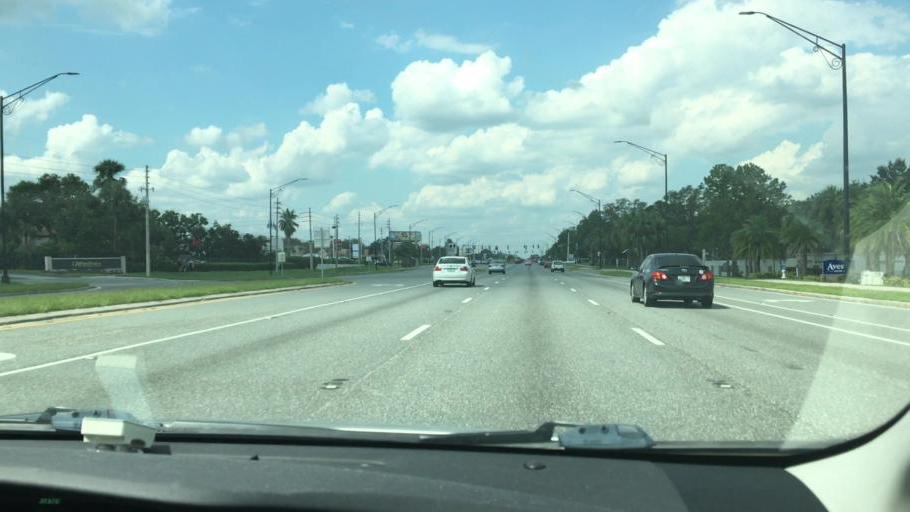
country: US
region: Florida
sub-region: Orange County
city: Conway
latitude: 28.5120
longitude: -81.3102
